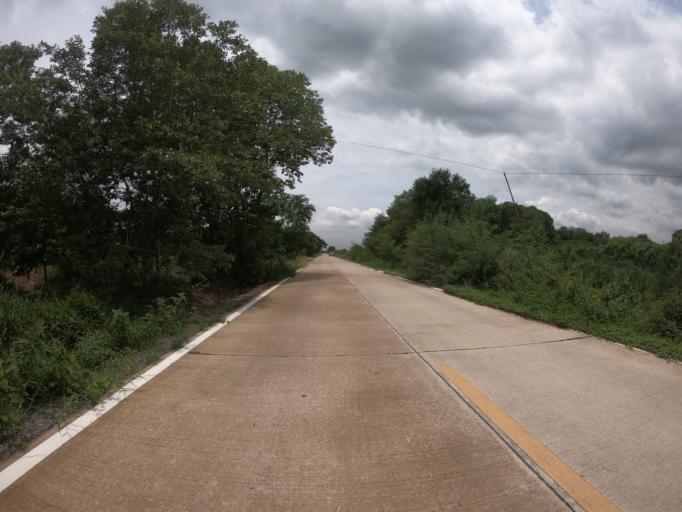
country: TH
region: Pathum Thani
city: Ban Lam Luk Ka
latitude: 13.9759
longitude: 100.8530
